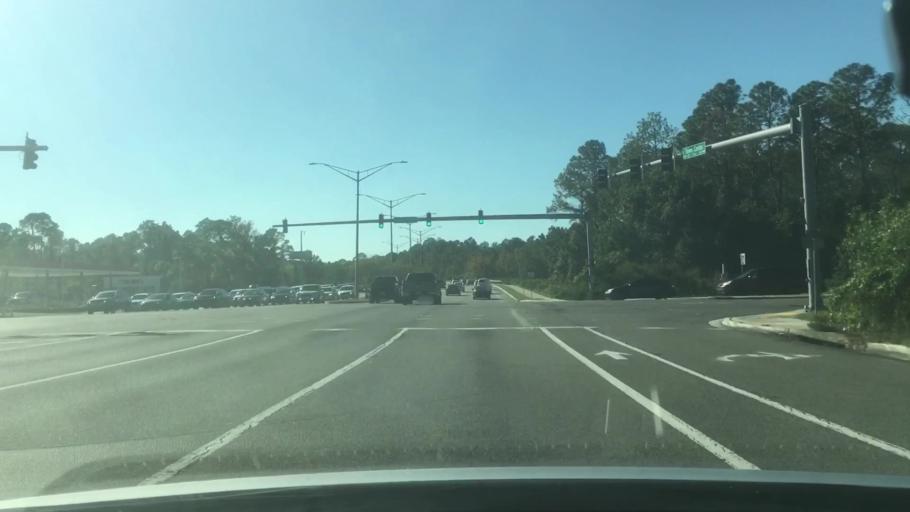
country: US
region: Florida
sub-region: Duval County
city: Jacksonville Beach
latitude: 30.2680
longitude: -81.5230
